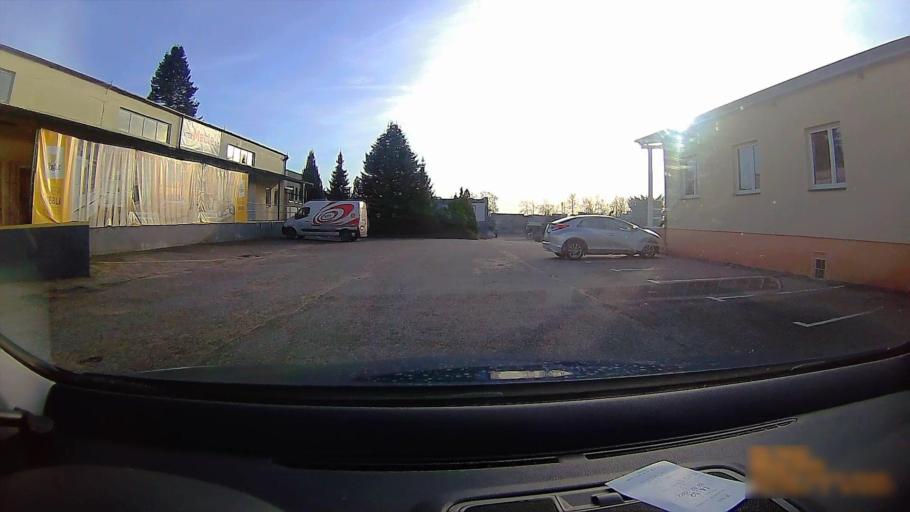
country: PL
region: Greater Poland Voivodeship
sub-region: Konin
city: Konin
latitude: 52.2322
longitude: 18.2373
